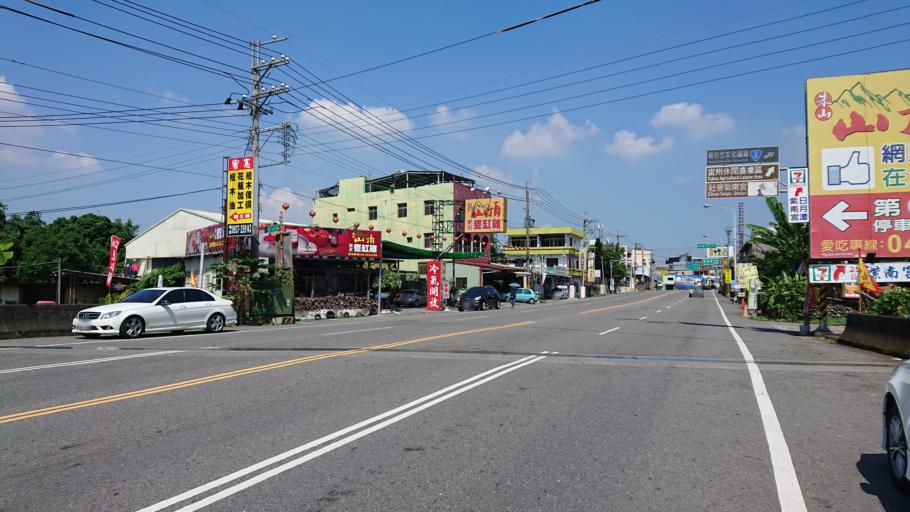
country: TW
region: Taiwan
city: Lugu
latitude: 23.8016
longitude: 120.7144
